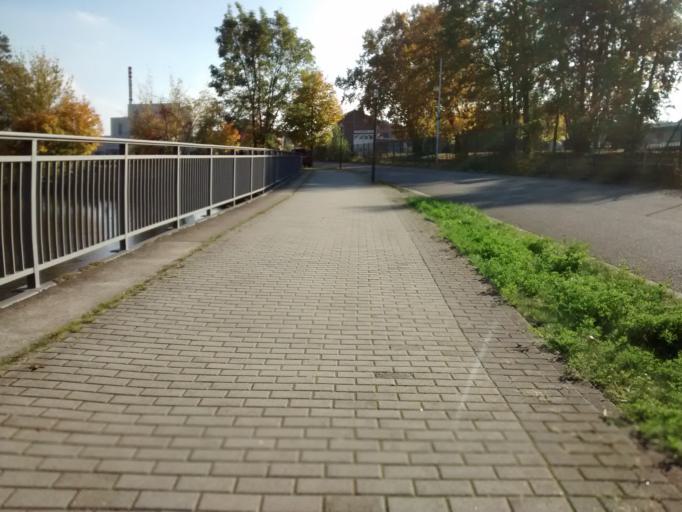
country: DE
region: Brandenburg
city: Hennigsdorf
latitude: 52.6305
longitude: 13.2138
